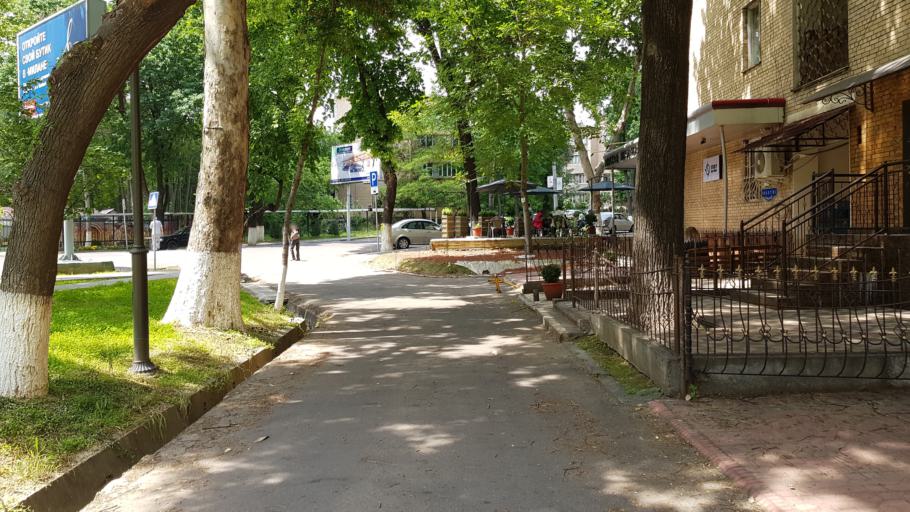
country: UZ
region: Toshkent Shahri
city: Tashkent
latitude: 41.3129
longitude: 69.2920
